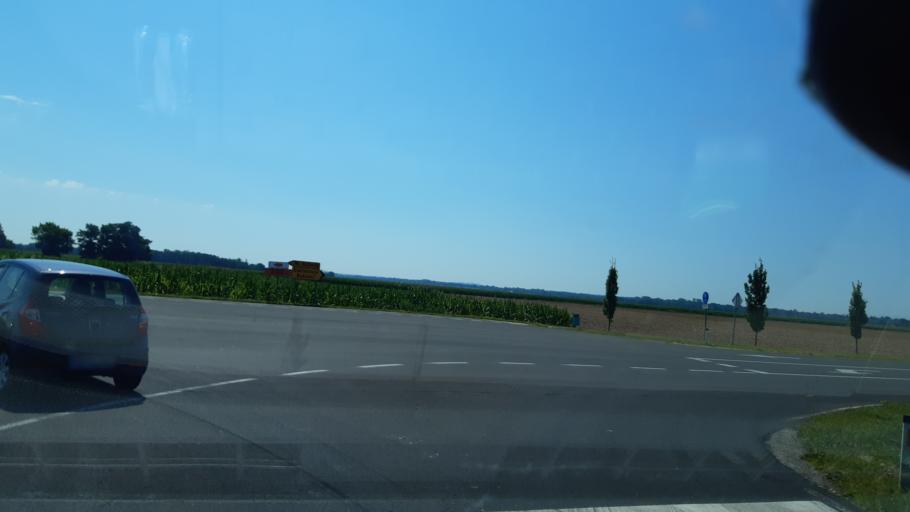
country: SI
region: Murska Sobota
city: Bakovci
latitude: 46.6298
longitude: 16.1556
